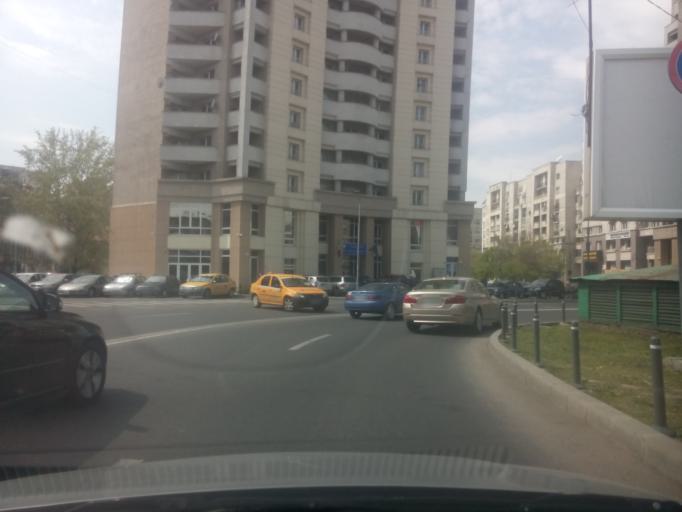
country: RO
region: Bucuresti
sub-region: Municipiul Bucuresti
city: Bucuresti
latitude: 44.4297
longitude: 26.0957
